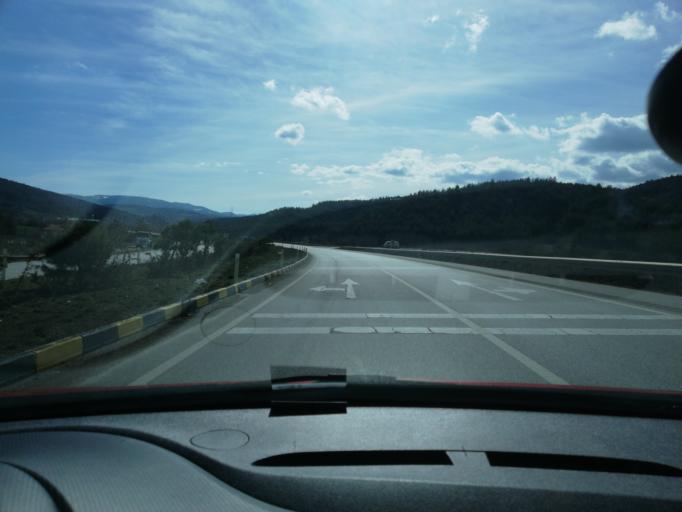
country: TR
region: Karabuk
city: Eskipazar
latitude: 40.9862
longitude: 32.5627
